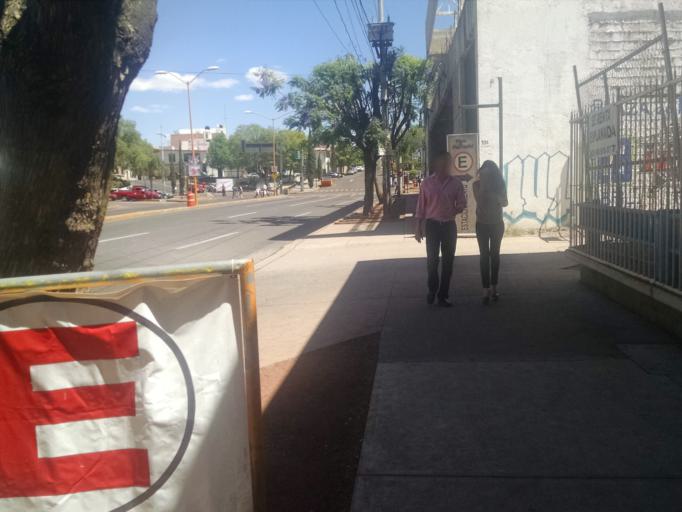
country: MX
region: Aguascalientes
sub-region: Aguascalientes
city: Aguascalientes
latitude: 21.8762
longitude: -102.3009
